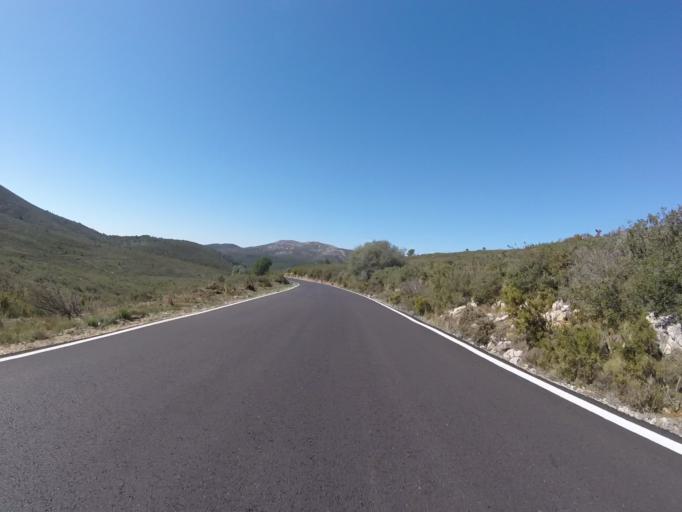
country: ES
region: Valencia
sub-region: Provincia de Castello
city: Cervera del Maestre
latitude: 40.4057
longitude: 0.2153
